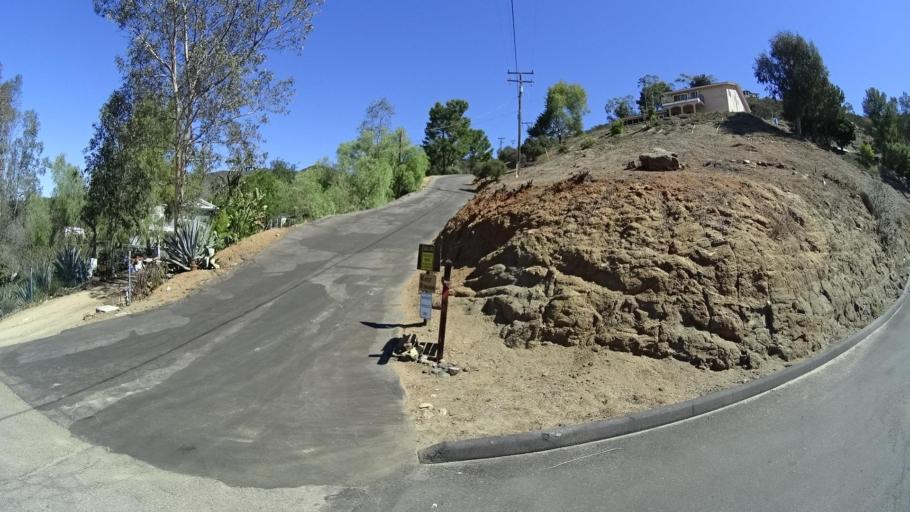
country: US
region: California
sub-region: San Diego County
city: Jamul
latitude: 32.7385
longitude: -116.8707
